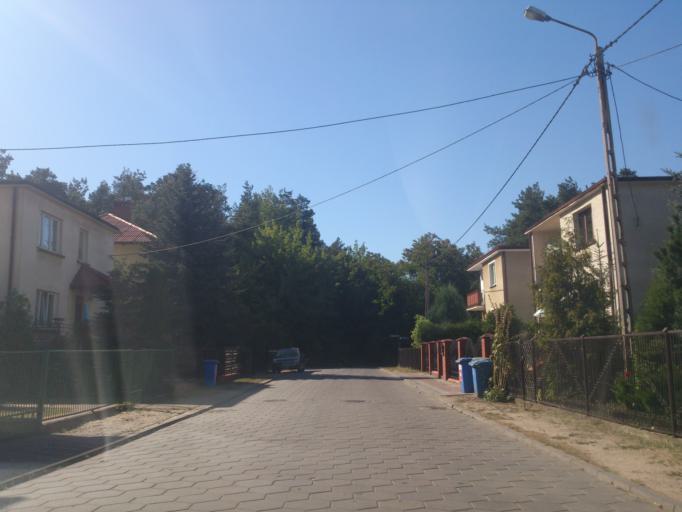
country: PL
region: Kujawsko-Pomorskie
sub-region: Powiat golubsko-dobrzynski
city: Golub-Dobrzyn
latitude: 53.1026
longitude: 19.0464
